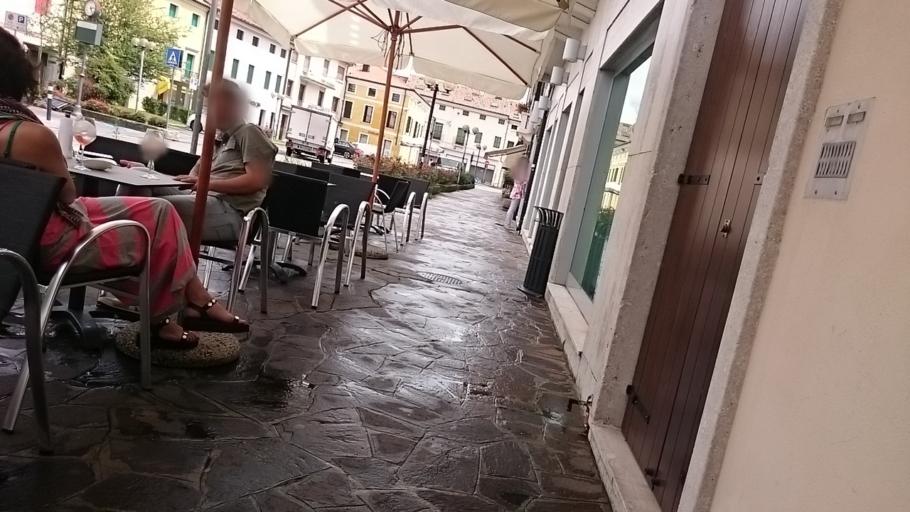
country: IT
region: Veneto
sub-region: Provincia di Padova
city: Camposampiero
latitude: 45.5714
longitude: 11.9316
